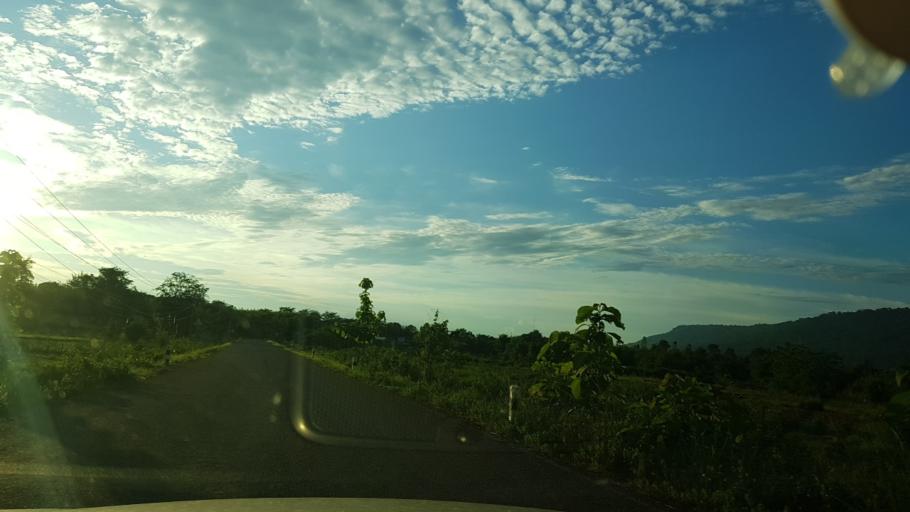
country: TH
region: Nong Khai
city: Sangkhom
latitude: 18.1267
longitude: 102.2851
